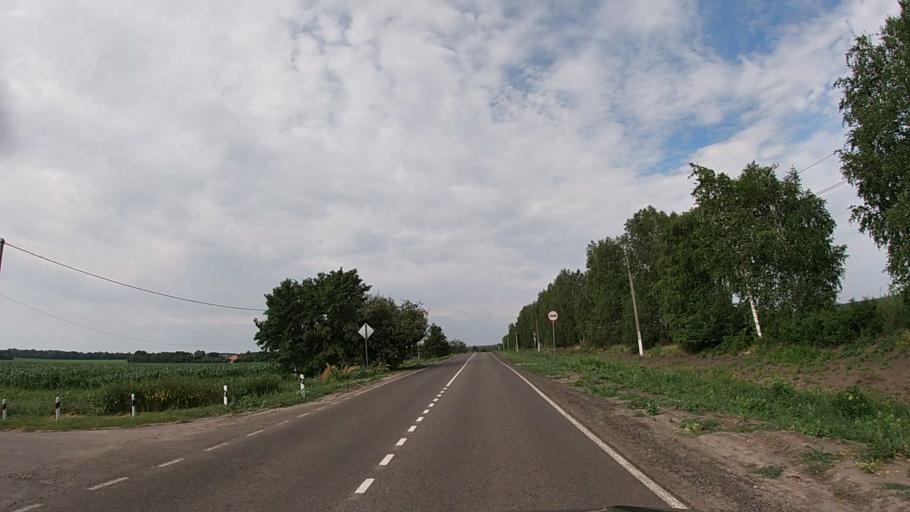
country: UA
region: Sumy
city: Krasnopillya
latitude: 50.8181
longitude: 35.4521
